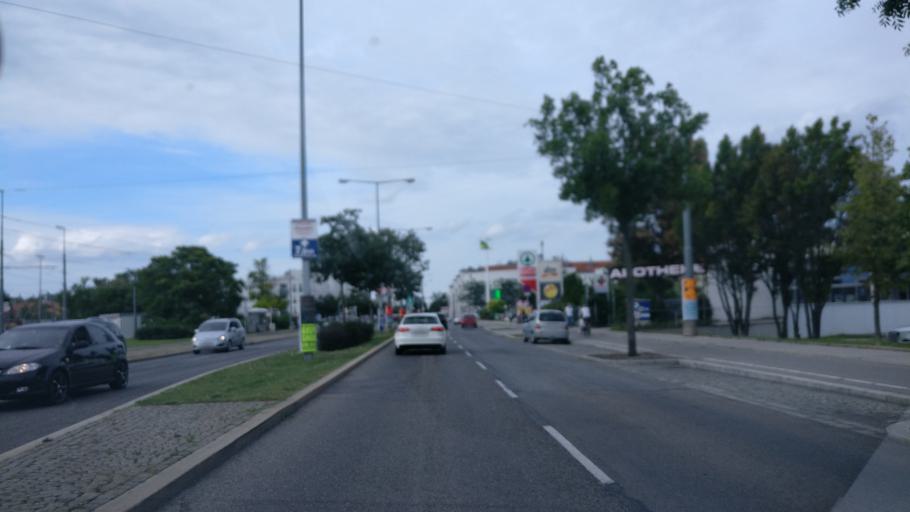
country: AT
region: Lower Austria
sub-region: Politischer Bezirk Korneuburg
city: Hagenbrunn
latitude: 48.2826
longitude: 16.4123
